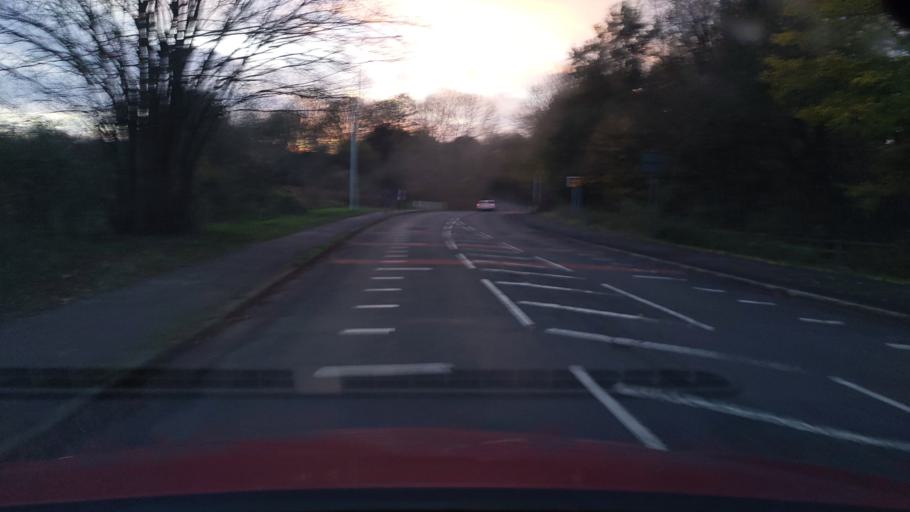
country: GB
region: England
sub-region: Lancashire
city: Clayton-le-Woods
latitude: 53.7003
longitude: -2.6550
